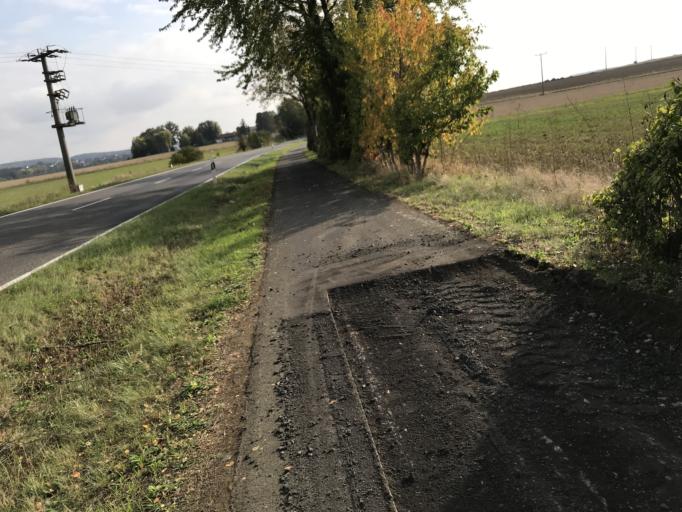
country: DE
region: Hesse
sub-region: Regierungsbezirk Giessen
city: Langgons
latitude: 50.5160
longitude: 8.6522
